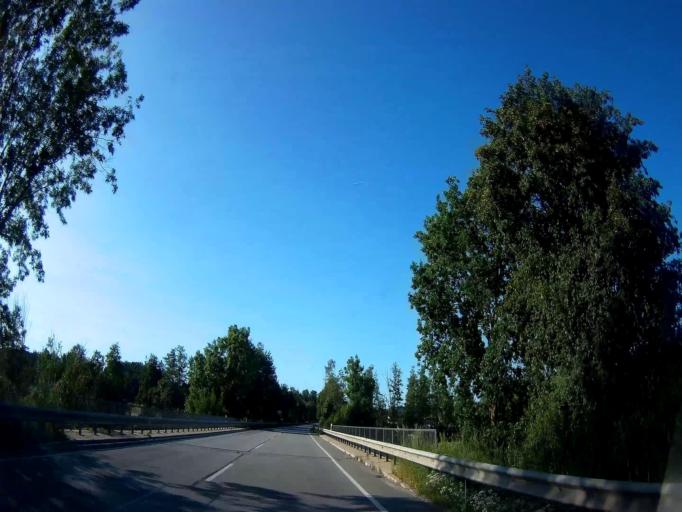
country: DE
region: Bavaria
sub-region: Lower Bavaria
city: Simbach
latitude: 48.6135
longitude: 12.7106
